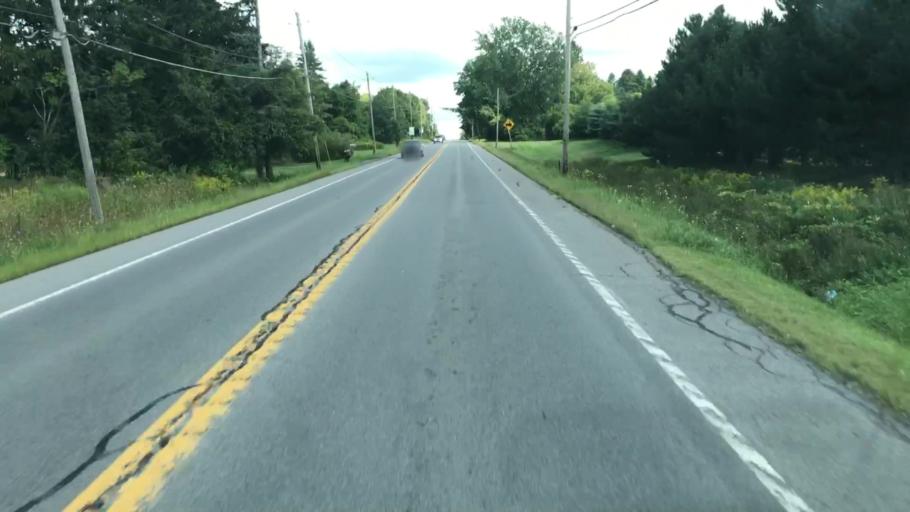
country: US
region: New York
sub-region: Onondaga County
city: Marcellus
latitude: 42.9837
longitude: -76.3102
